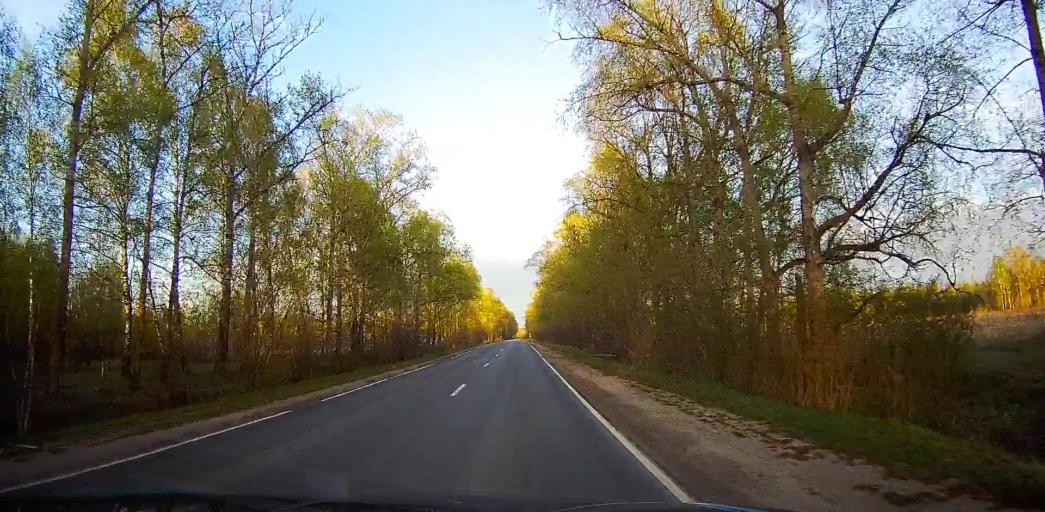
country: RU
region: Moskovskaya
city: Peski
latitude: 55.2087
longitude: 38.7200
